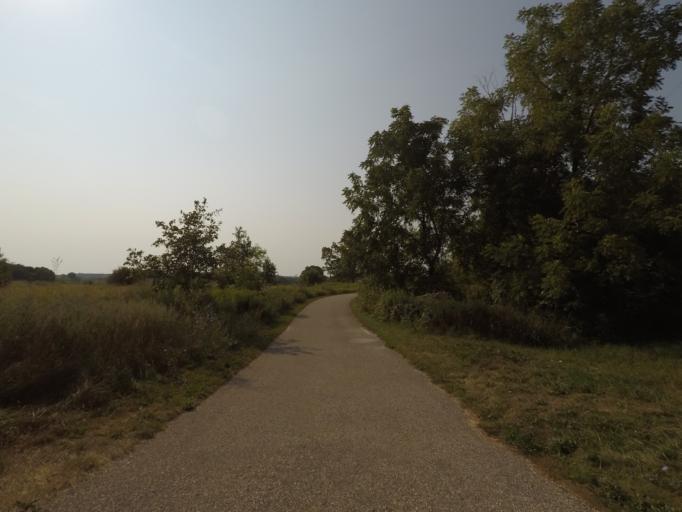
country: US
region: Wisconsin
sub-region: Waukesha County
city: Delafield
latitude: 43.0517
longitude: -88.4140
